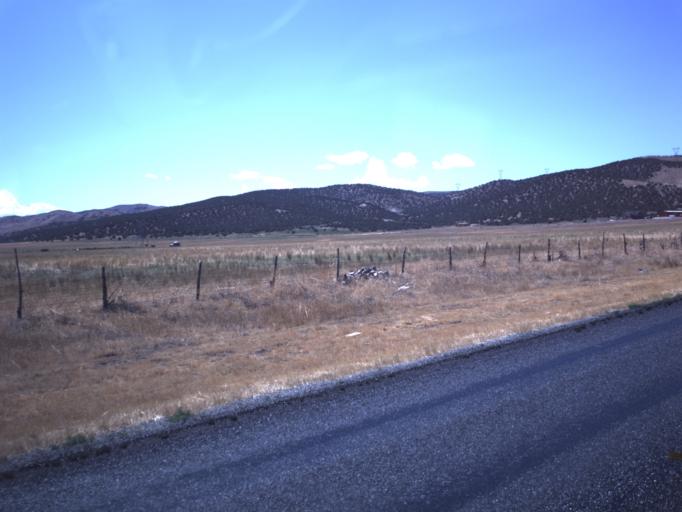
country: US
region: Utah
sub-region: Juab County
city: Nephi
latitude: 39.7061
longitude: -111.9110
